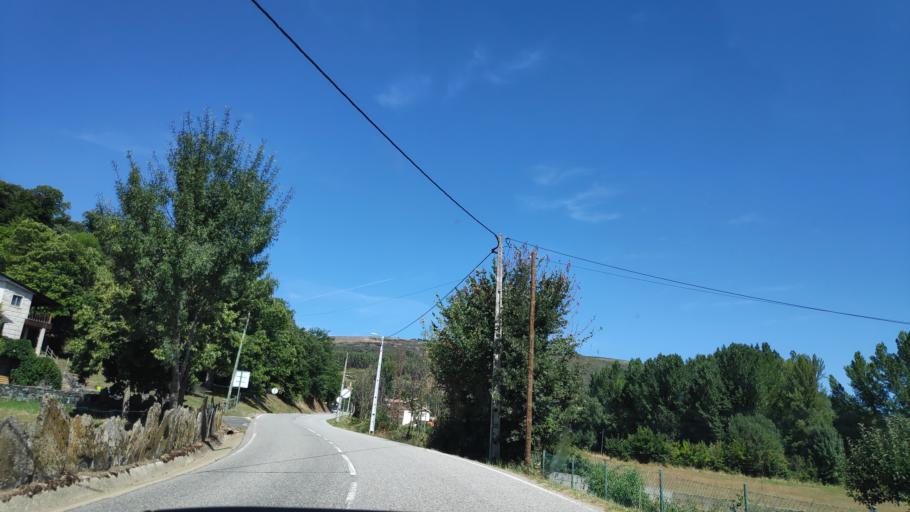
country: PT
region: Braganca
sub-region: Braganca Municipality
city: Braganca
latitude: 41.8668
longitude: -6.7488
